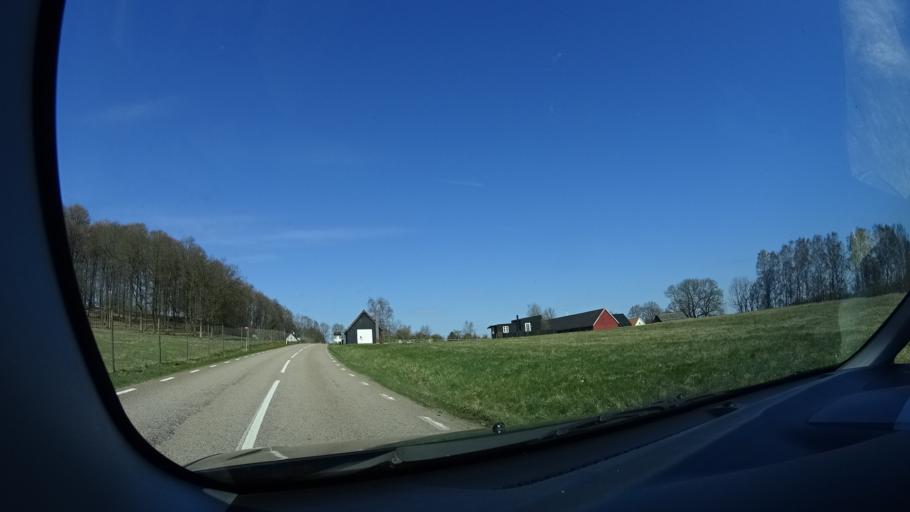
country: SE
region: Skane
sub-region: Klippans Kommun
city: Klippan
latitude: 56.1012
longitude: 13.1066
